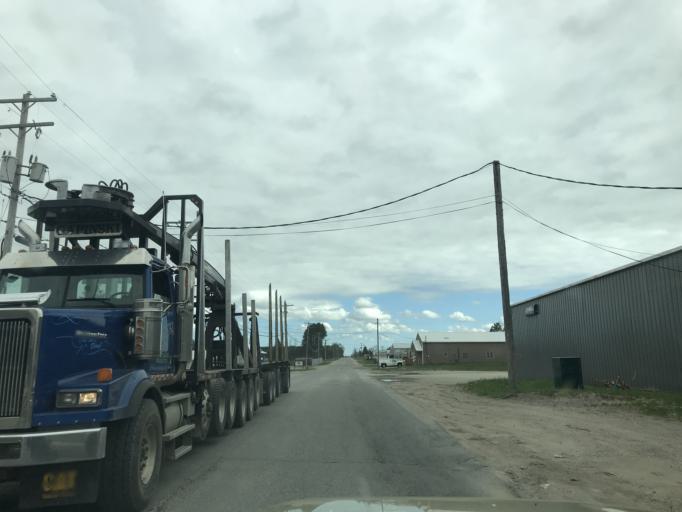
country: US
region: Michigan
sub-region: Otsego County
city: Gaylord
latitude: 45.0280
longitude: -84.6941
